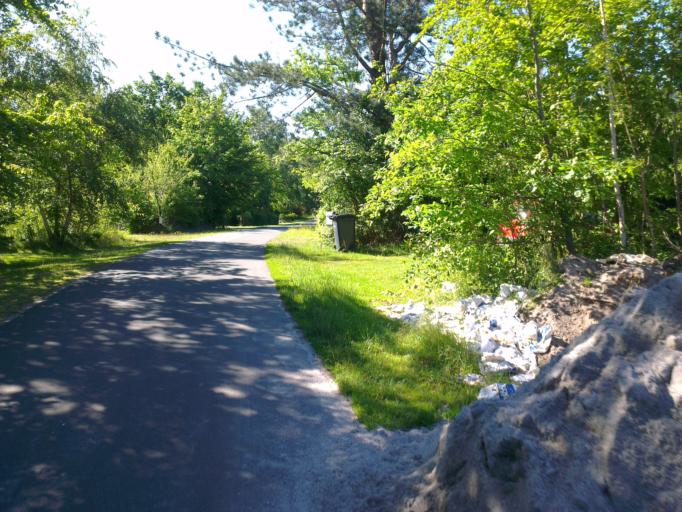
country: DK
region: Capital Region
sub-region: Halsnaes Kommune
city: Hundested
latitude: 55.9227
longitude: 11.9072
